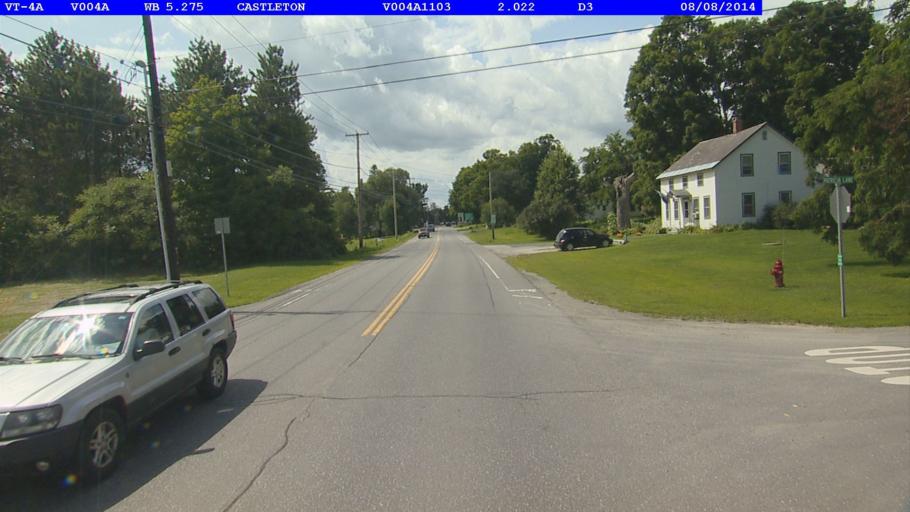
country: US
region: Vermont
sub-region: Rutland County
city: Castleton
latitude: 43.6080
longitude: -73.2043
